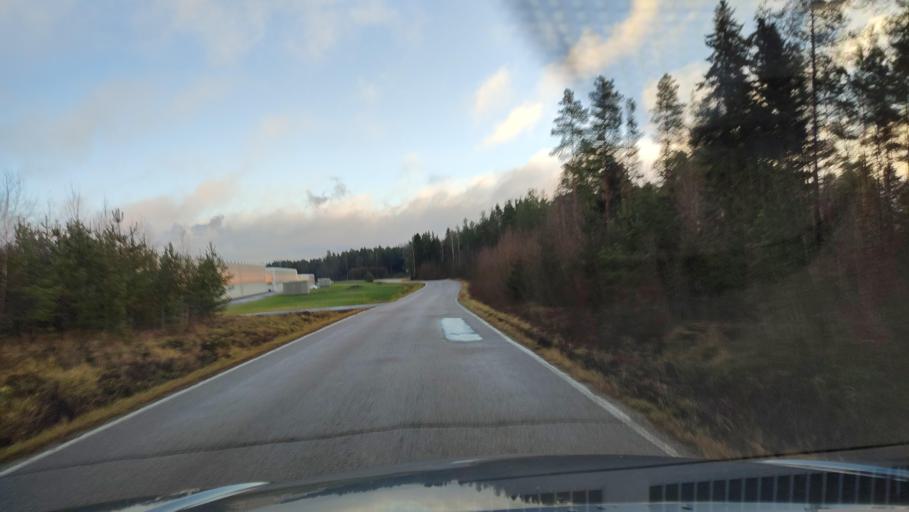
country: FI
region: Ostrobothnia
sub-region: Sydosterbotten
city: Naerpes
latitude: 62.4431
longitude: 21.3982
